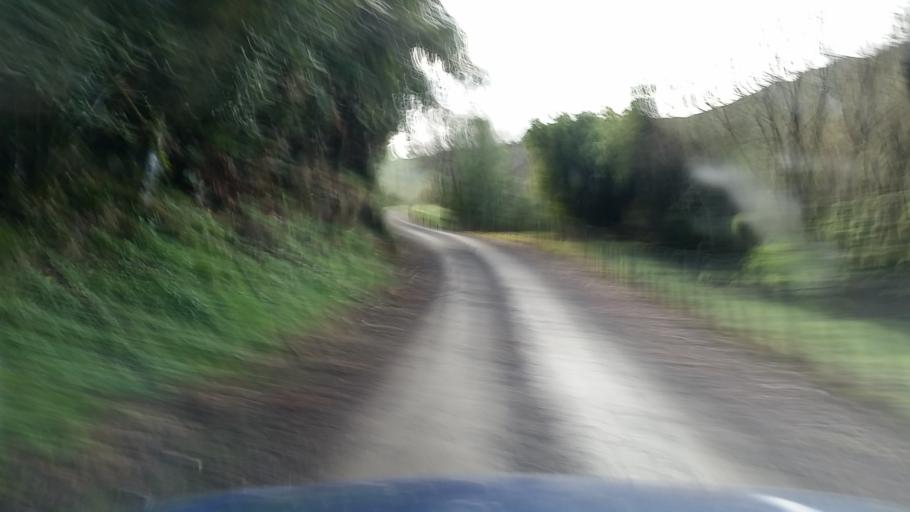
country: NZ
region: Taranaki
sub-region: New Plymouth District
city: Waitara
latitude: -39.0980
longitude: 174.8379
